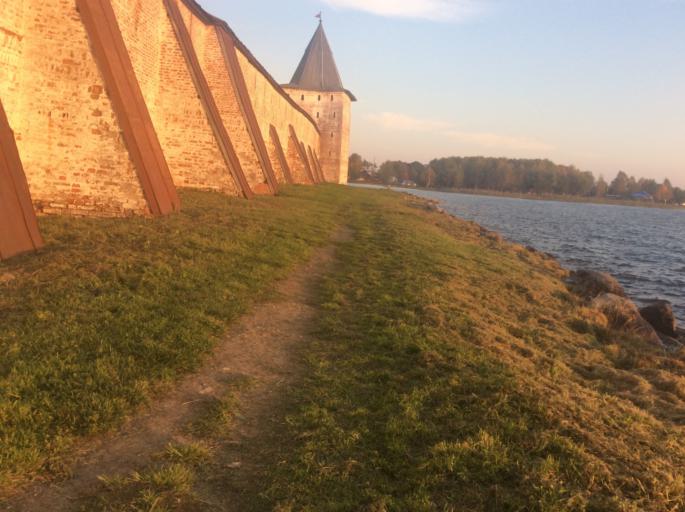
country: RU
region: Vologda
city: Kirillov
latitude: 59.8567
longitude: 38.3658
